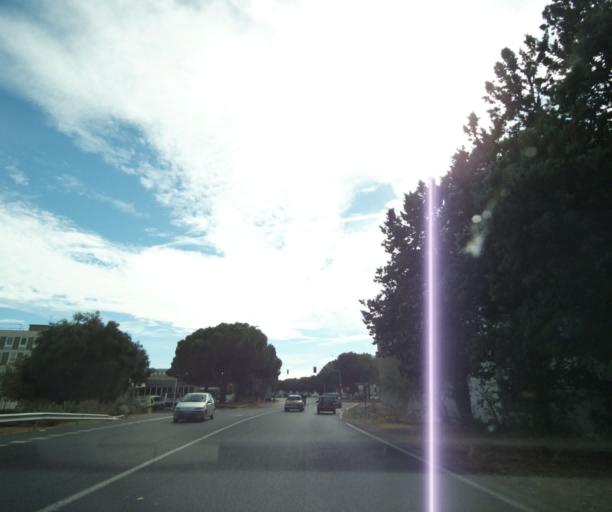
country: FR
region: Languedoc-Roussillon
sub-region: Departement de l'Herault
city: Montpellier
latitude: 43.6055
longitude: 3.8648
